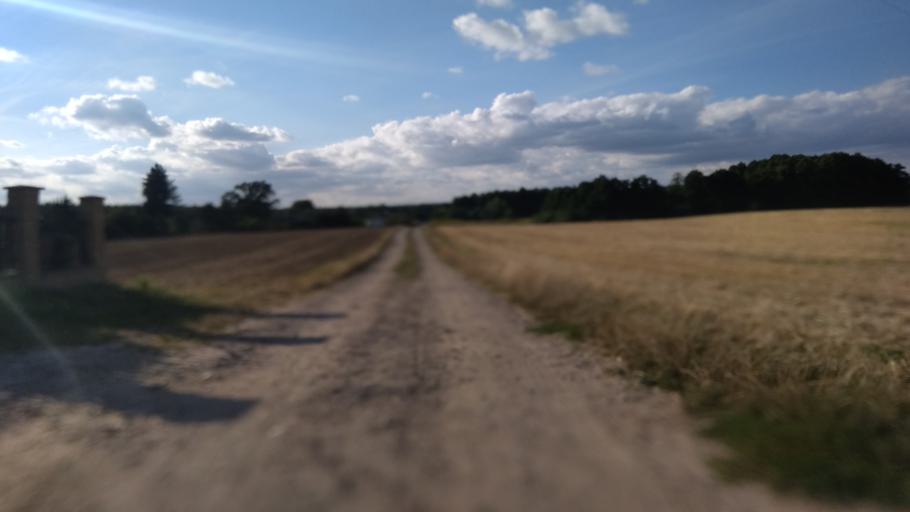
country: PL
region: Kujawsko-Pomorskie
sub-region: Powiat bydgoski
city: Osielsko
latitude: 53.2282
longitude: 18.1268
